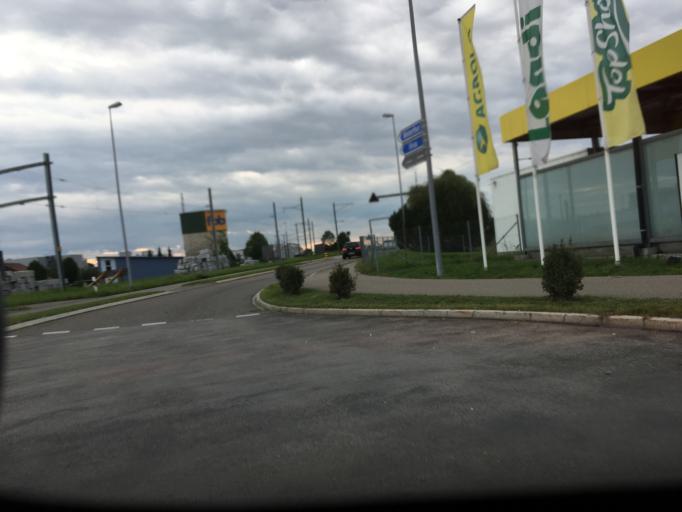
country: CH
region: Zurich
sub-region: Bezirk Pfaeffikon
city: Pfaeffikon / Pfaeffikon (Dorfkern)
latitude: 47.3715
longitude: 8.7755
